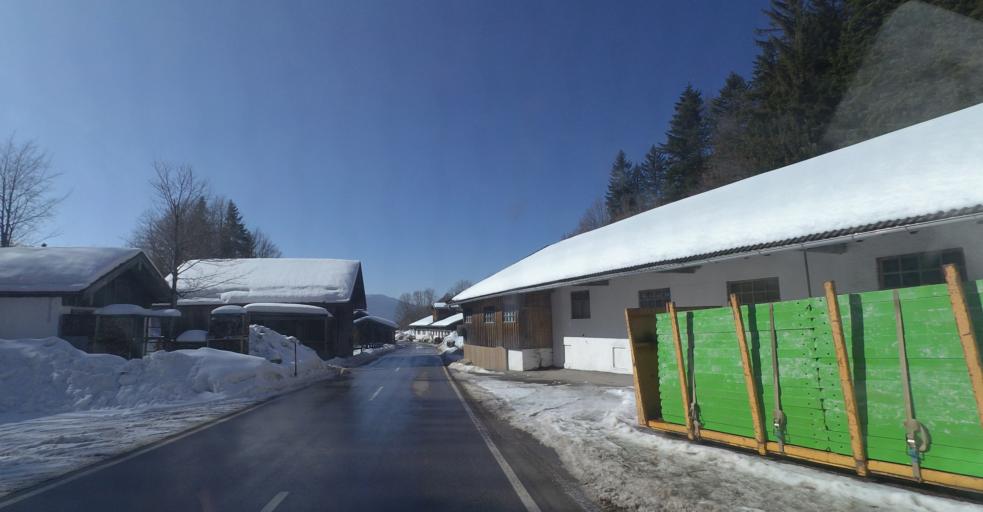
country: DE
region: Bavaria
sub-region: Upper Bavaria
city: Inzell
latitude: 47.7721
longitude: 12.7826
